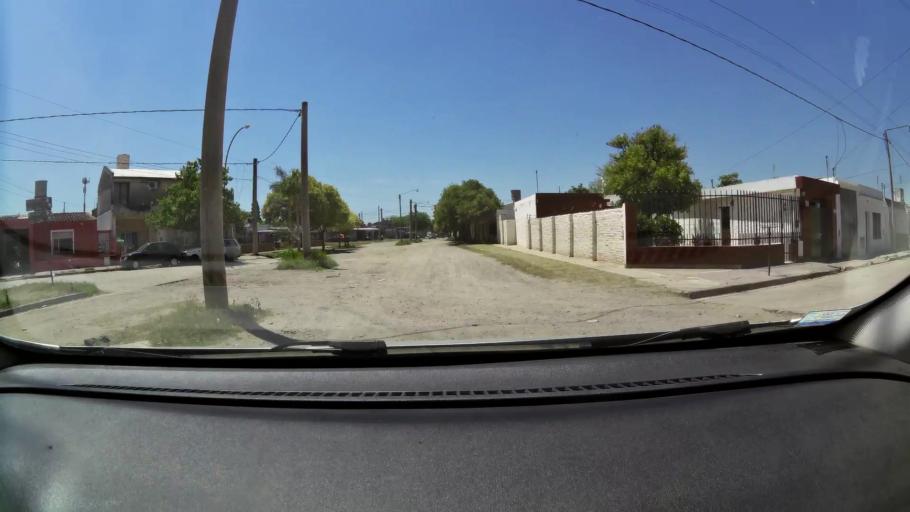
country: AR
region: Cordoba
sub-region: Departamento de Capital
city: Cordoba
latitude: -31.3867
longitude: -64.1479
